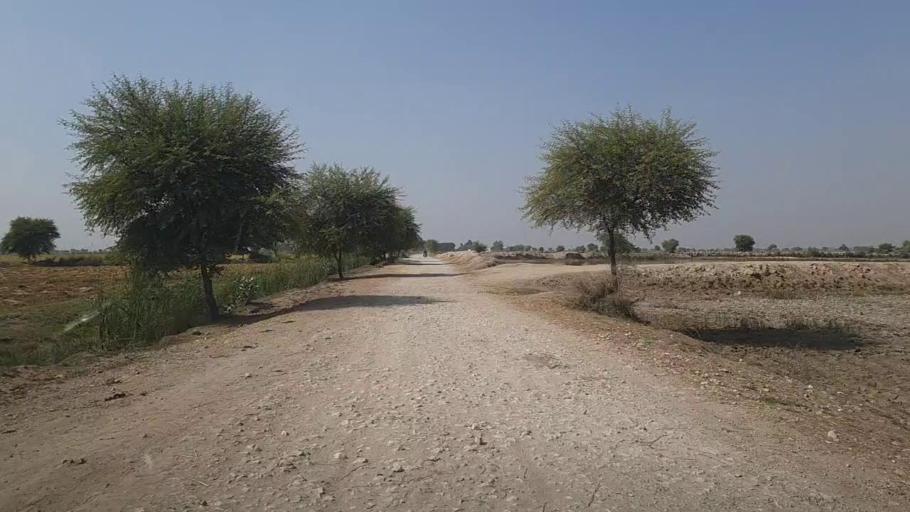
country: PK
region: Sindh
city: Kandhkot
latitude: 28.3932
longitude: 69.3012
